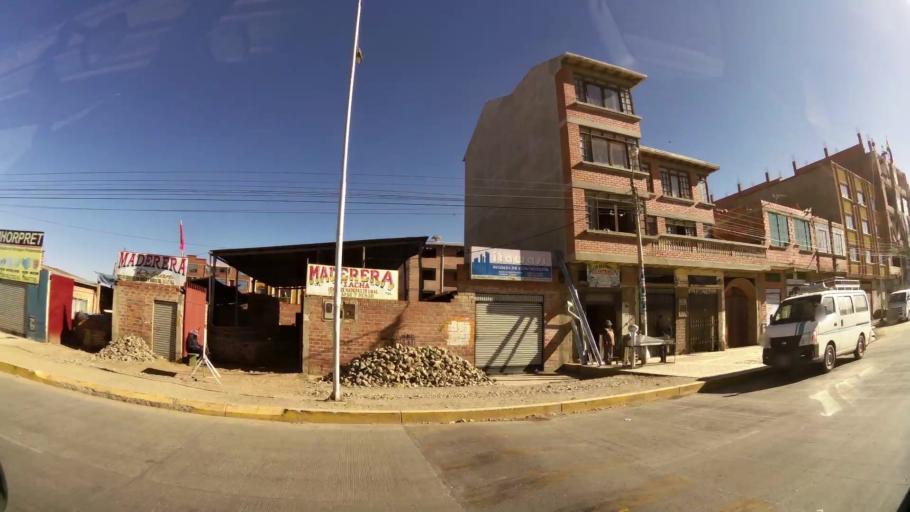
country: BO
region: La Paz
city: La Paz
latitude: -16.5322
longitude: -68.1887
